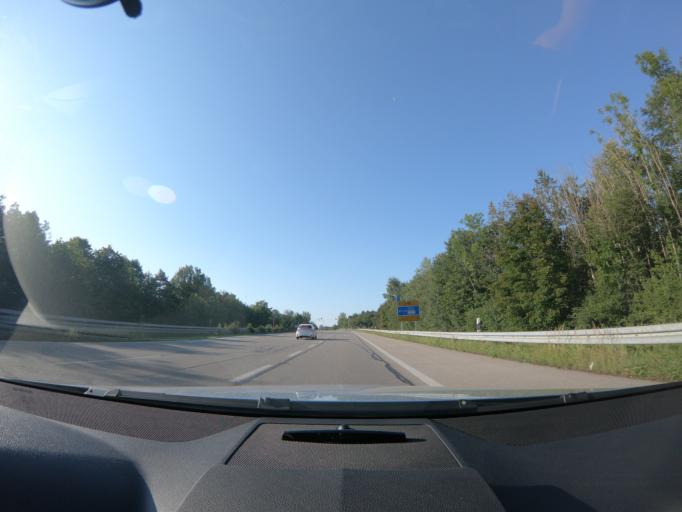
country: DE
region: Bavaria
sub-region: Upper Bavaria
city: Oberschleissheim
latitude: 48.2255
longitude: 11.5874
